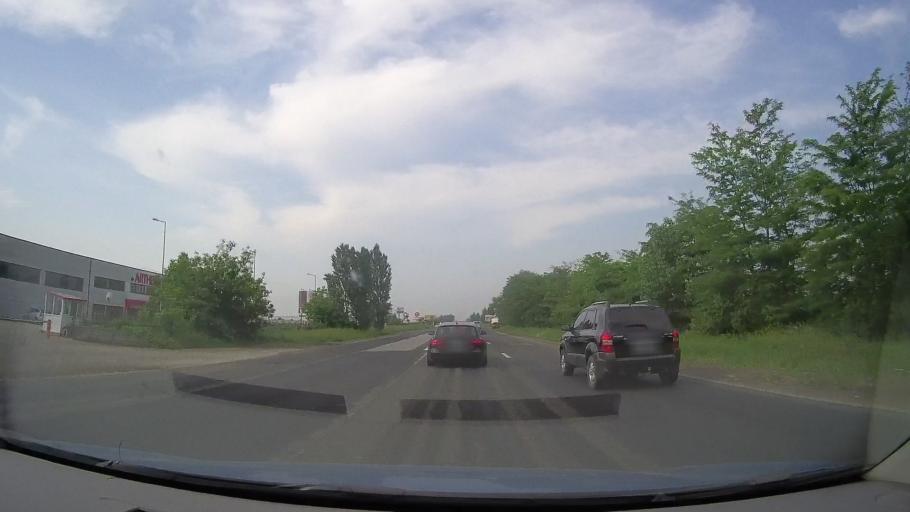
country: RO
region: Timis
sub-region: Comuna Giroc
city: Chisoda
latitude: 45.7098
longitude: 21.1897
